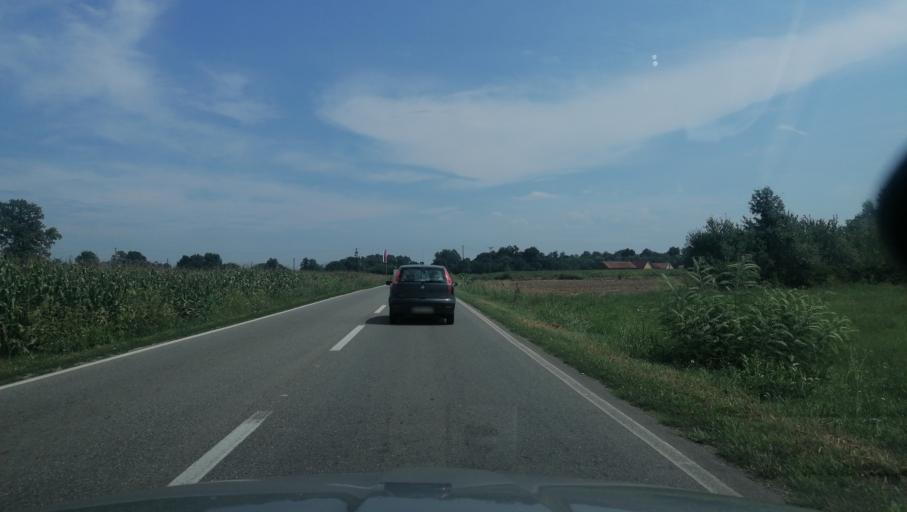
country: BA
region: Republika Srpska
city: Velika Obarska
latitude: 44.8261
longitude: 19.0358
